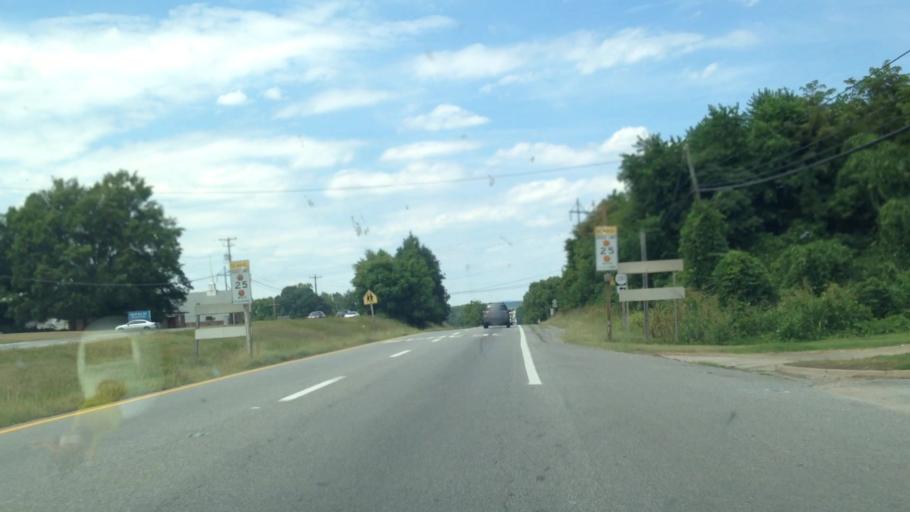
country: US
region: Virginia
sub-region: Henry County
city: Chatmoss
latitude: 36.6036
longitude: -79.8616
